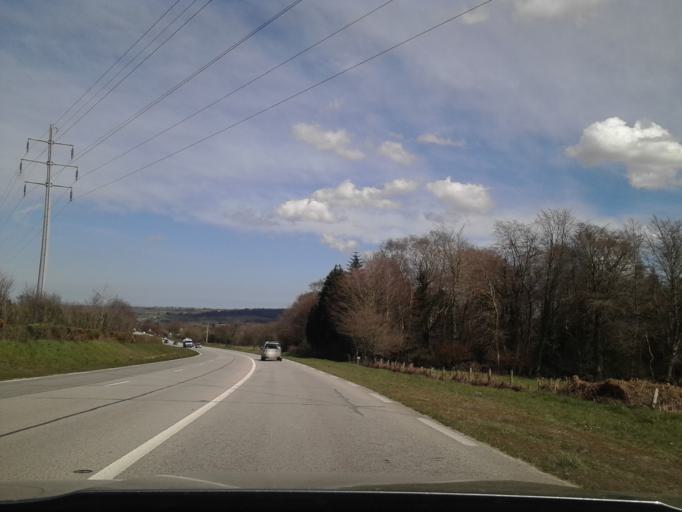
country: FR
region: Lower Normandy
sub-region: Departement de la Manche
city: La Glacerie
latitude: 49.6081
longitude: -1.5886
